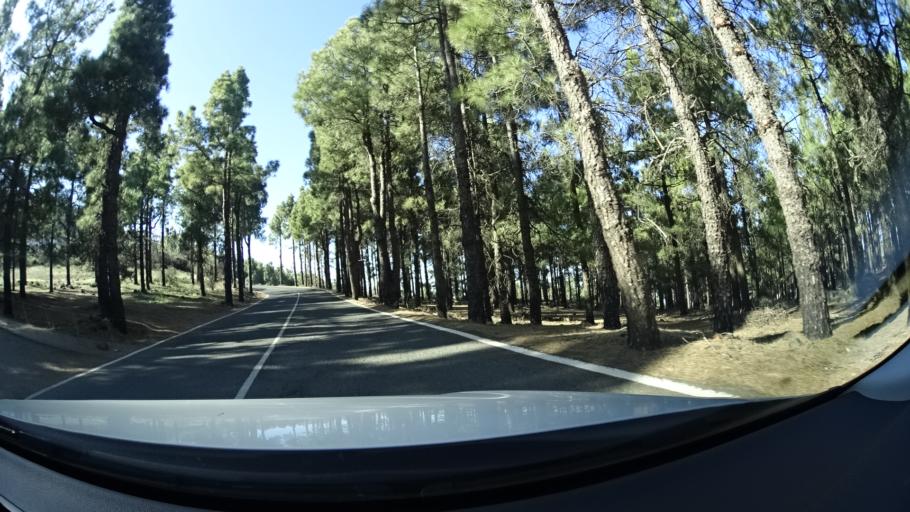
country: ES
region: Canary Islands
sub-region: Provincia de Las Palmas
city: San Bartolome
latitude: 27.9661
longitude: -15.5601
